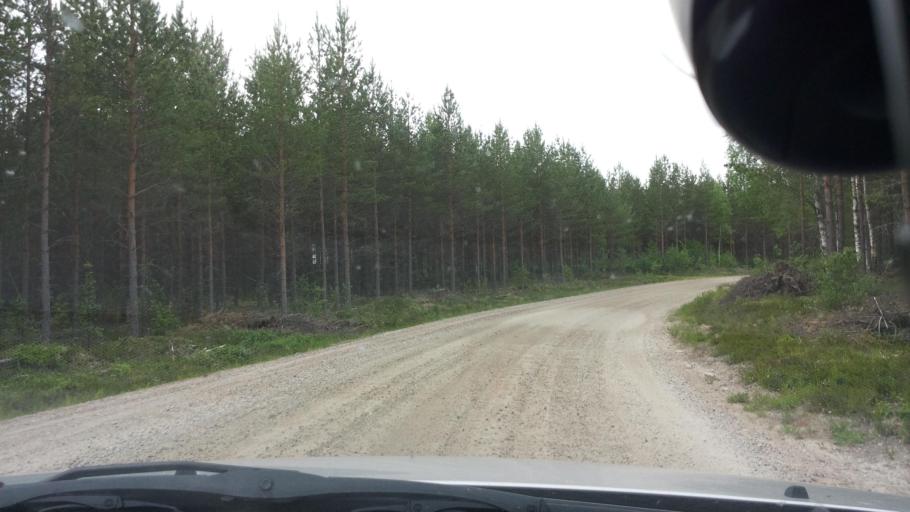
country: SE
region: Gaevleborg
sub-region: Ovanakers Kommun
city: Edsbyn
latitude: 61.5152
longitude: 15.3543
